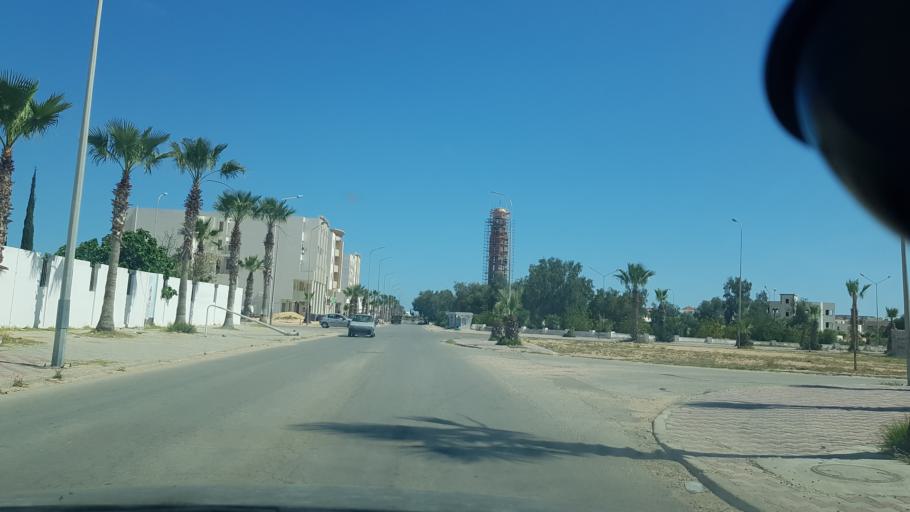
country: TN
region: Safaqis
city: Al Qarmadah
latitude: 34.8287
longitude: 10.7580
